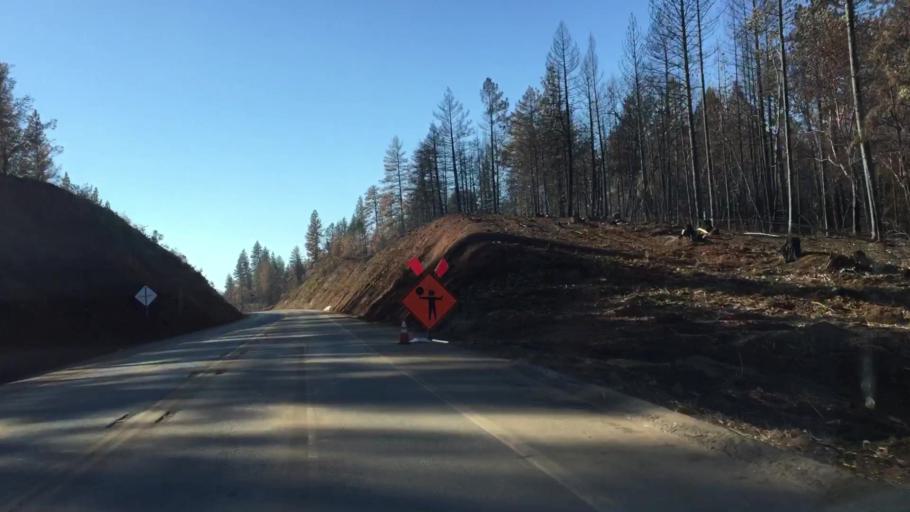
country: US
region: California
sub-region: Butte County
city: Magalia
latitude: 39.7225
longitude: -121.5113
